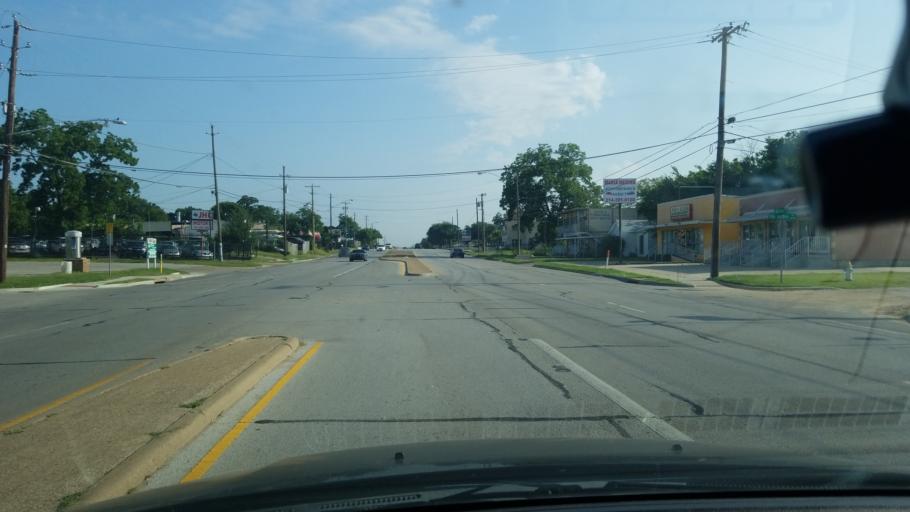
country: US
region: Texas
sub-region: Dallas County
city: Balch Springs
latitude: 32.7287
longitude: -96.6829
